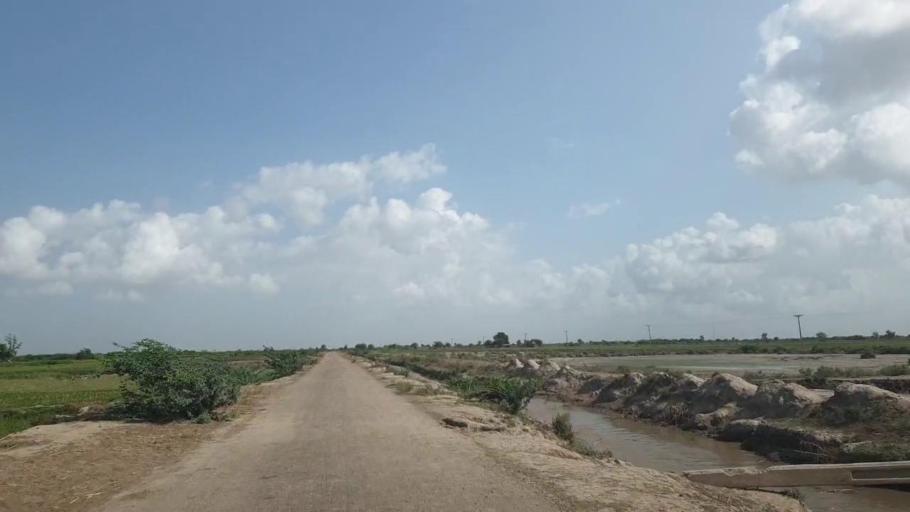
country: PK
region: Sindh
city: Kadhan
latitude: 24.5704
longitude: 69.0673
